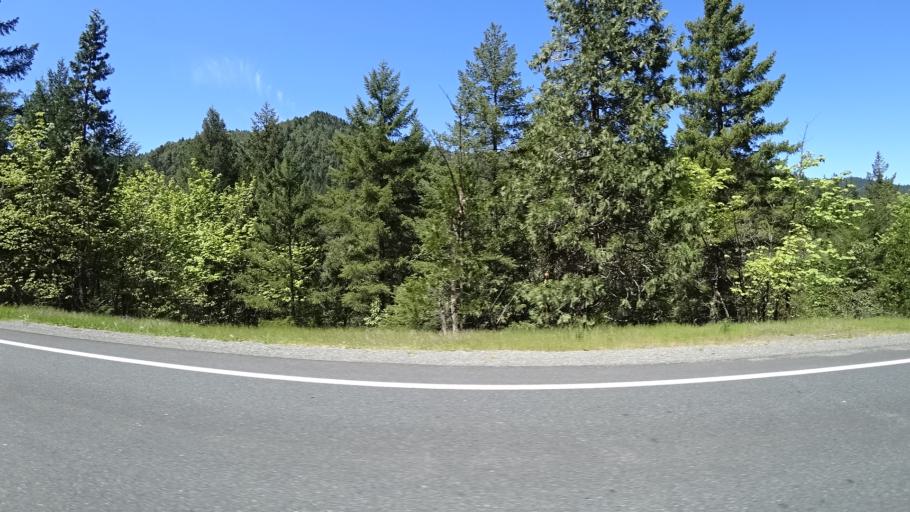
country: US
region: California
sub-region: Humboldt County
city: Willow Creek
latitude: 40.9344
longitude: -123.6737
